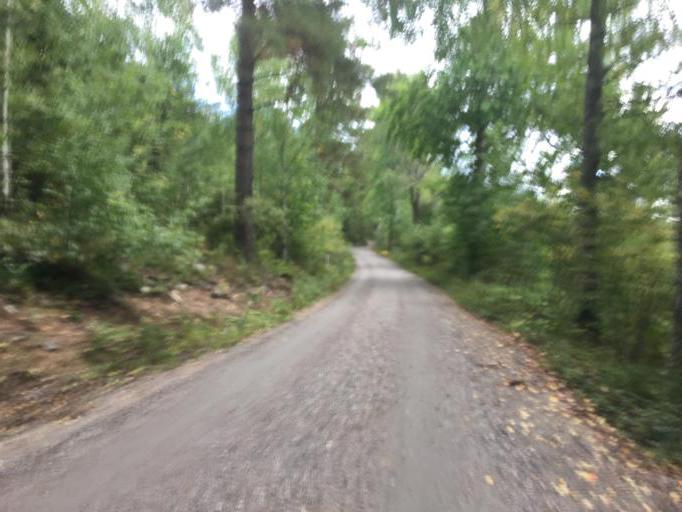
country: SE
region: Soedermanland
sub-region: Eskilstuna Kommun
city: Arla
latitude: 59.4560
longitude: 16.6804
